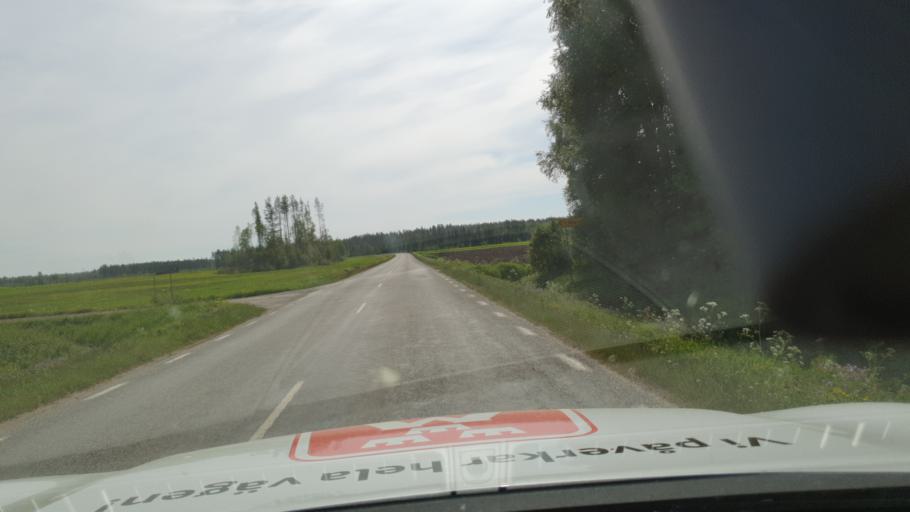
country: SE
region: Vaesterbotten
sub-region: Robertsfors Kommun
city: Robertsfors
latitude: 64.2963
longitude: 20.8886
